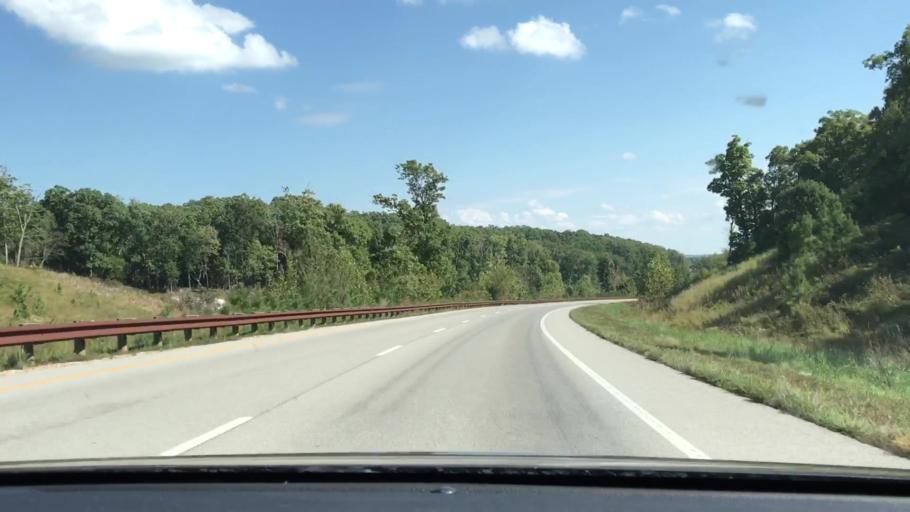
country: US
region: Kentucky
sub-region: Trigg County
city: Cadiz
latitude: 36.7830
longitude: -88.0413
